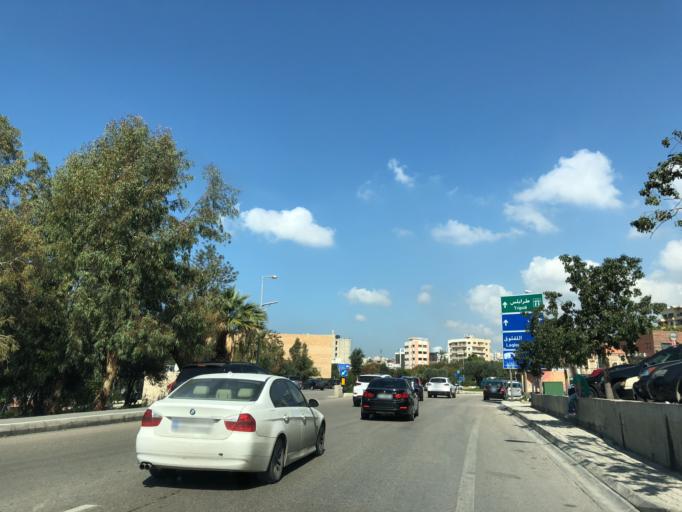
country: LB
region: Mont-Liban
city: Jbail
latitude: 34.1223
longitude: 35.6520
